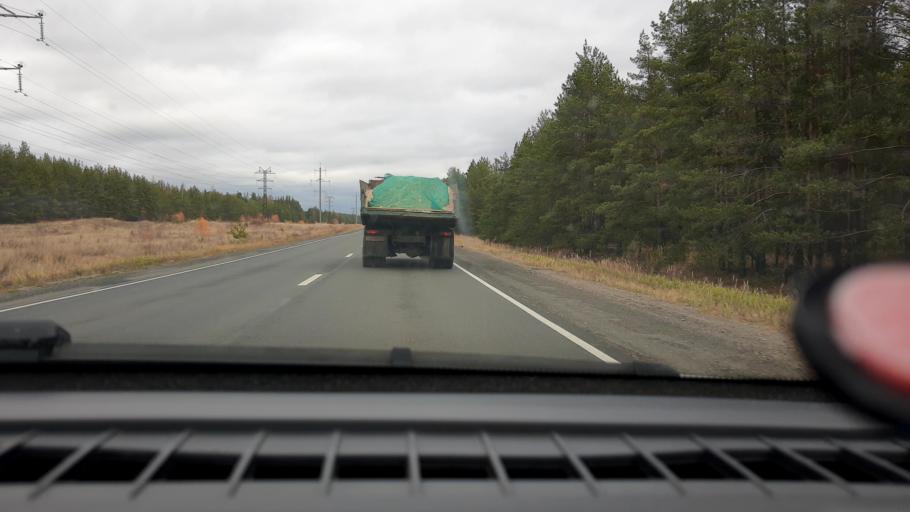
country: RU
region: Nizjnij Novgorod
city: Lukino
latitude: 56.3888
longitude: 43.6398
